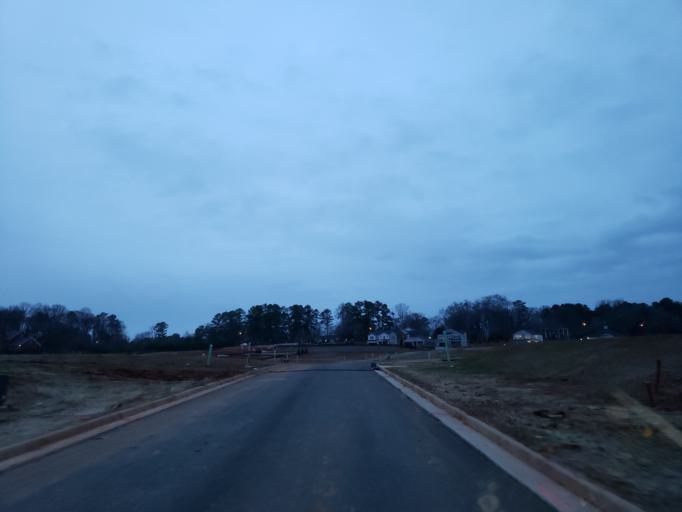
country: US
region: Georgia
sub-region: Cobb County
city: Mableton
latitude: 33.8374
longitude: -84.5812
